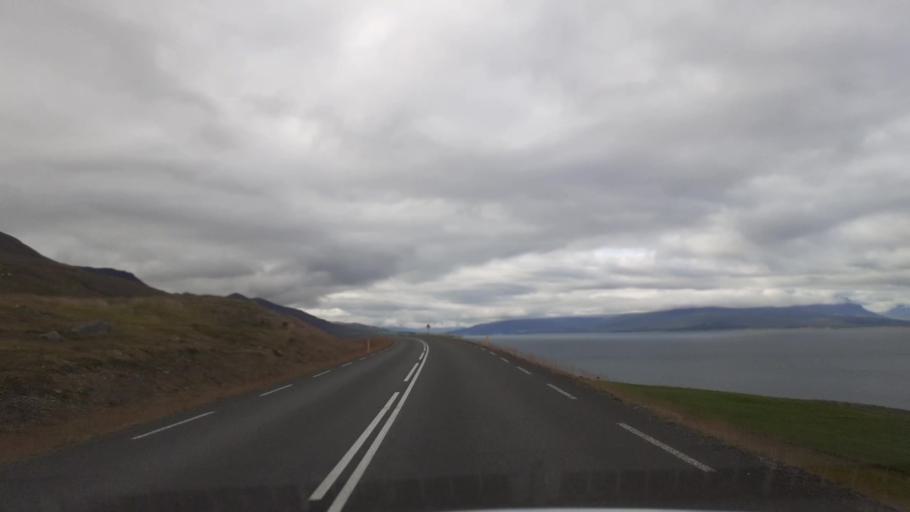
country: IS
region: Northeast
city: Akureyri
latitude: 65.8739
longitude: -18.0770
